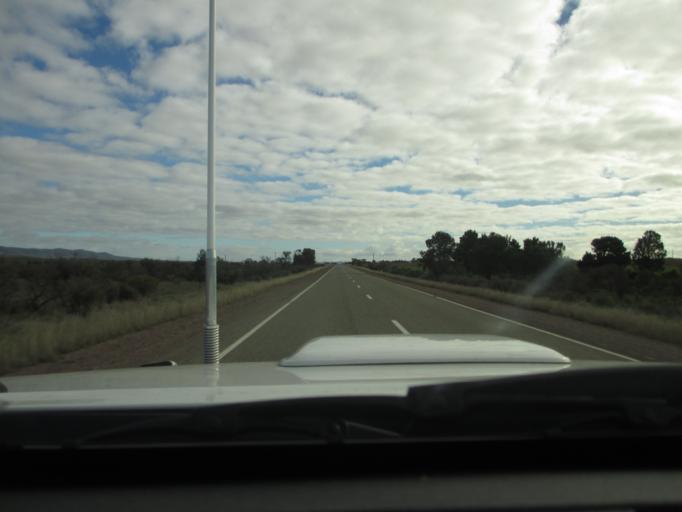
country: AU
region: South Australia
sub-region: Flinders Ranges
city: Quorn
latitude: -32.4354
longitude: 138.5340
